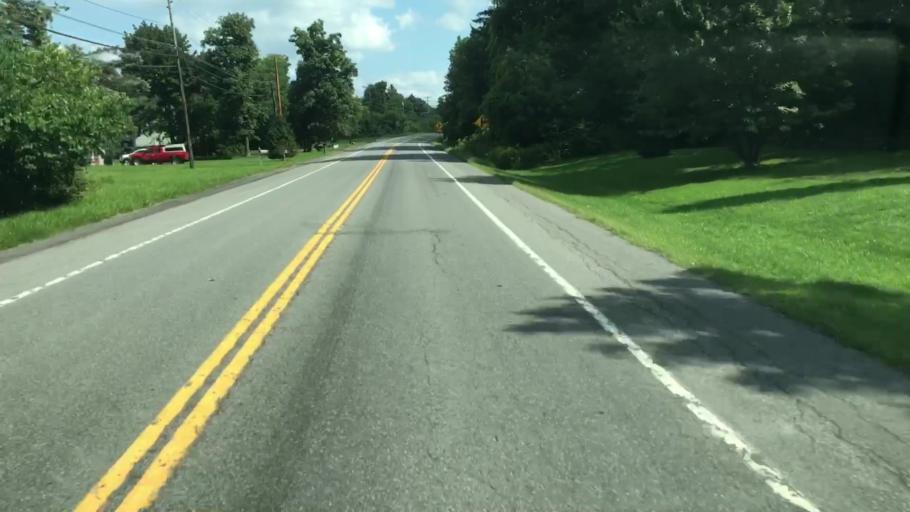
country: US
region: New York
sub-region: Onondaga County
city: Nedrow
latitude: 42.9948
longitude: -76.1005
